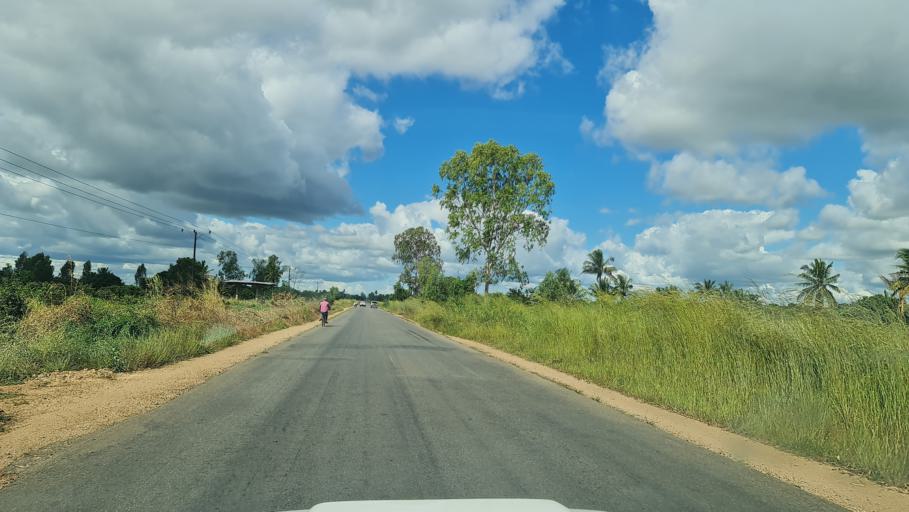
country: MZ
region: Zambezia
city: Quelimane
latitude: -17.5924
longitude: 36.7715
